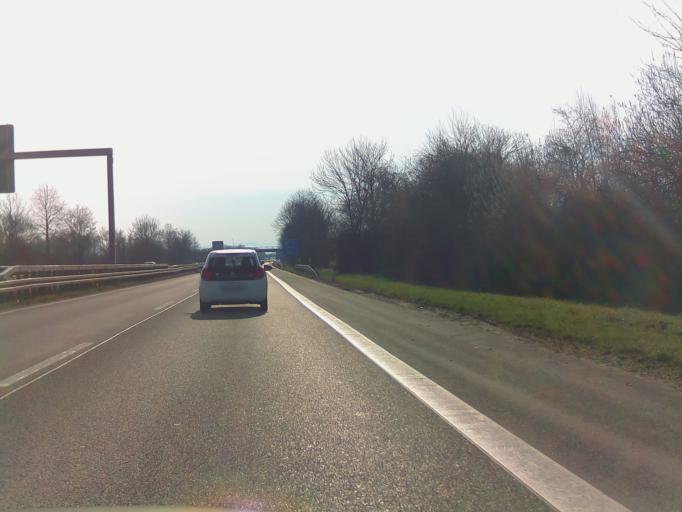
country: DE
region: Hesse
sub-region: Regierungsbezirk Darmstadt
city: Oberursel
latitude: 50.2146
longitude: 8.5807
